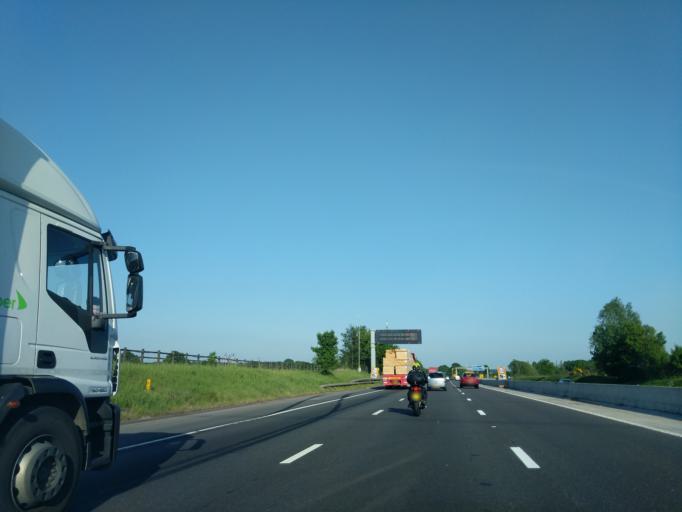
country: GB
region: England
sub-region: Cheshire East
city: Mere
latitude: 53.3214
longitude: -2.4393
